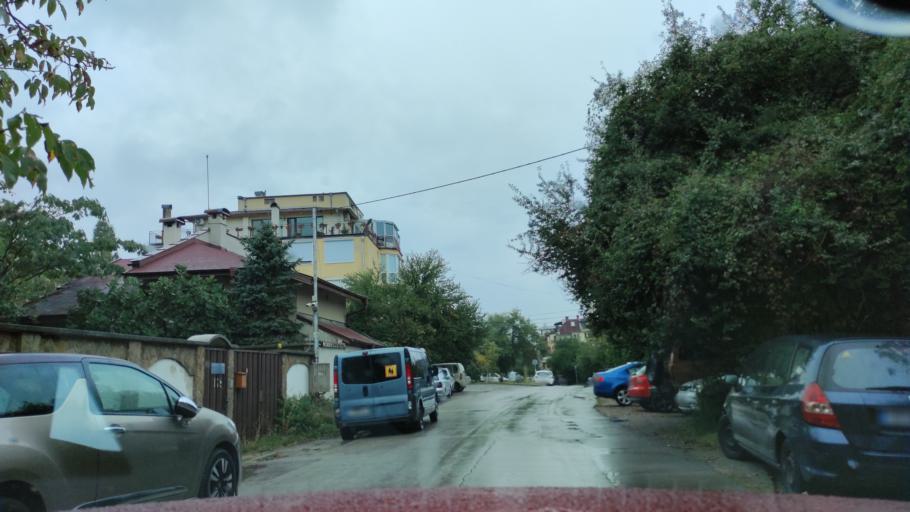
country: BG
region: Sofia-Capital
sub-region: Stolichna Obshtina
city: Sofia
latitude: 42.6595
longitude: 23.2784
